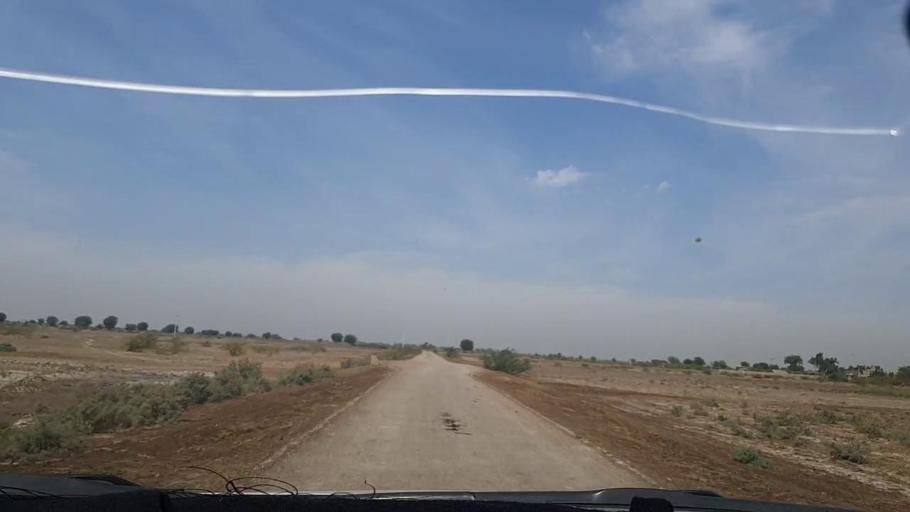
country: PK
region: Sindh
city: Pithoro
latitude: 25.4706
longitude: 69.4704
